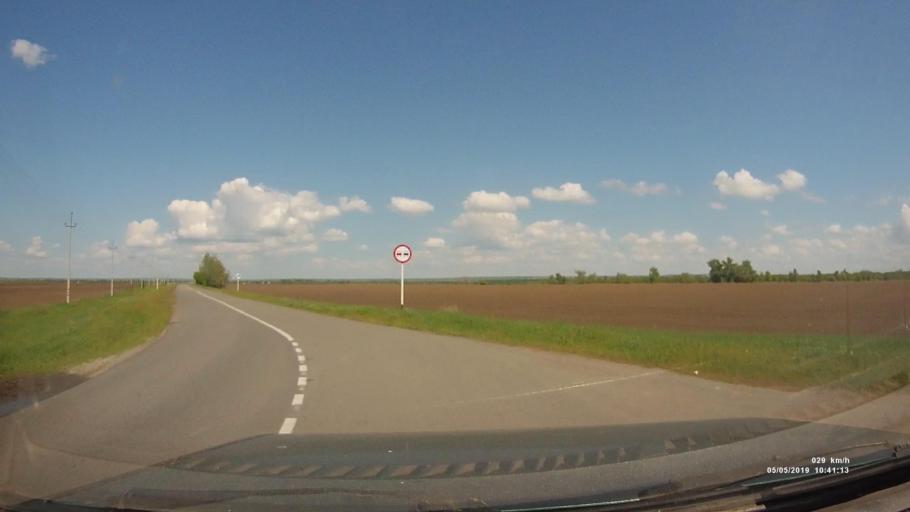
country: RU
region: Rostov
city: Ust'-Donetskiy
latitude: 47.5897
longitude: 40.8432
